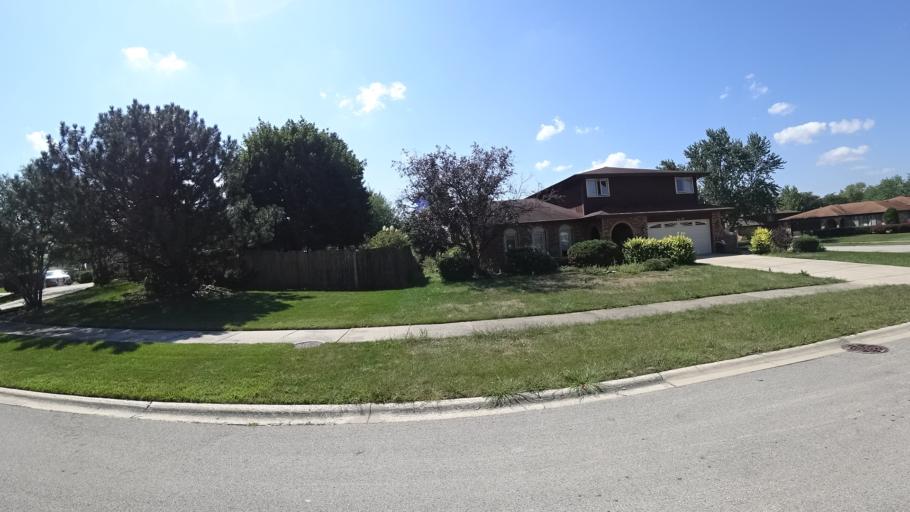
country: US
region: Illinois
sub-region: Cook County
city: Orland Park
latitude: 41.6340
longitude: -87.8424
